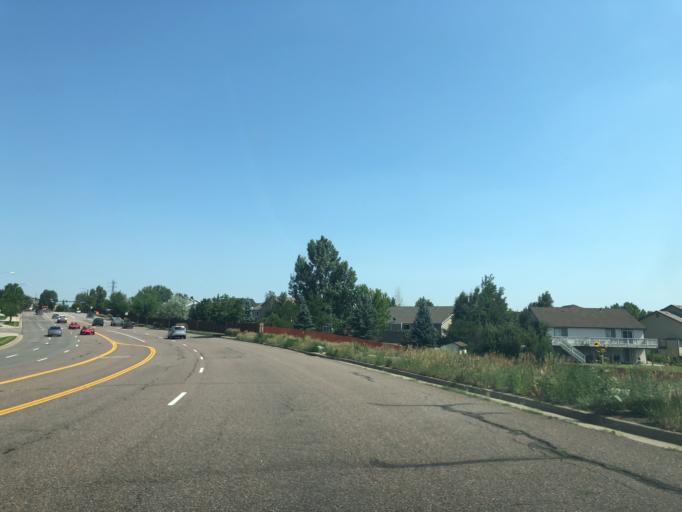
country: US
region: Colorado
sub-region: Arapahoe County
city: Dove Valley
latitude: 39.6353
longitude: -104.7627
